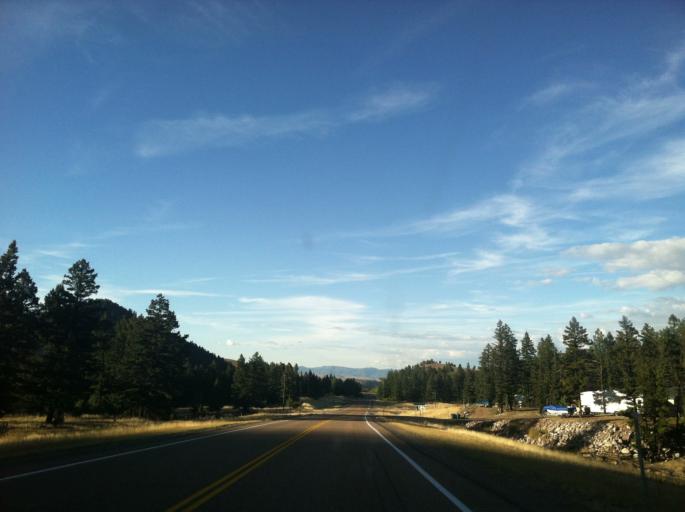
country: US
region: Montana
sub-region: Granite County
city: Philipsburg
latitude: 46.4607
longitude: -113.2348
